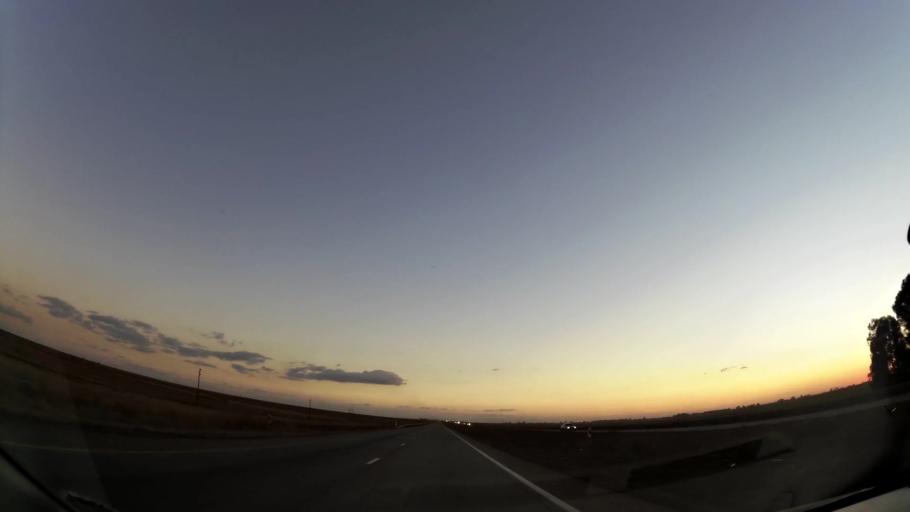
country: ZA
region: Mpumalanga
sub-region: Nkangala District Municipality
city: Witbank
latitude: -25.9779
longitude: 29.1713
